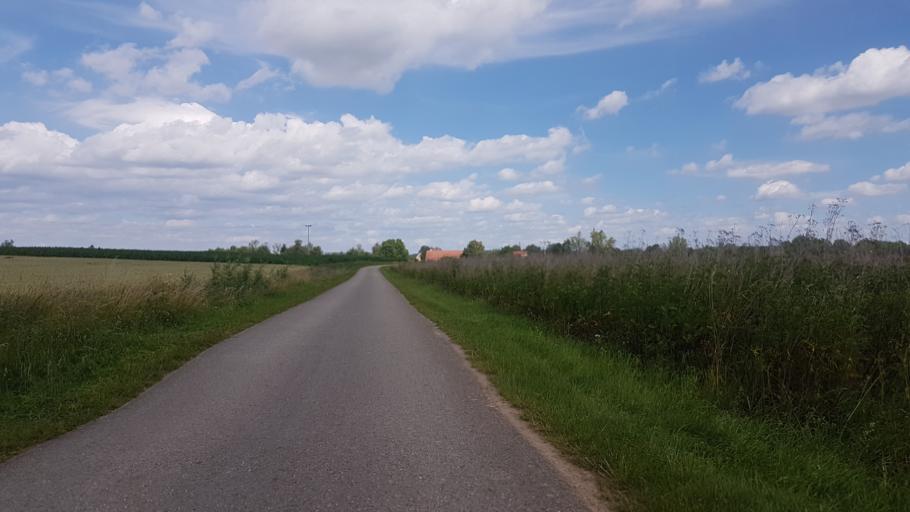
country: DE
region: Bavaria
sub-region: Regierungsbezirk Mittelfranken
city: Dittenheim
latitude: 49.0702
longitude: 10.8004
